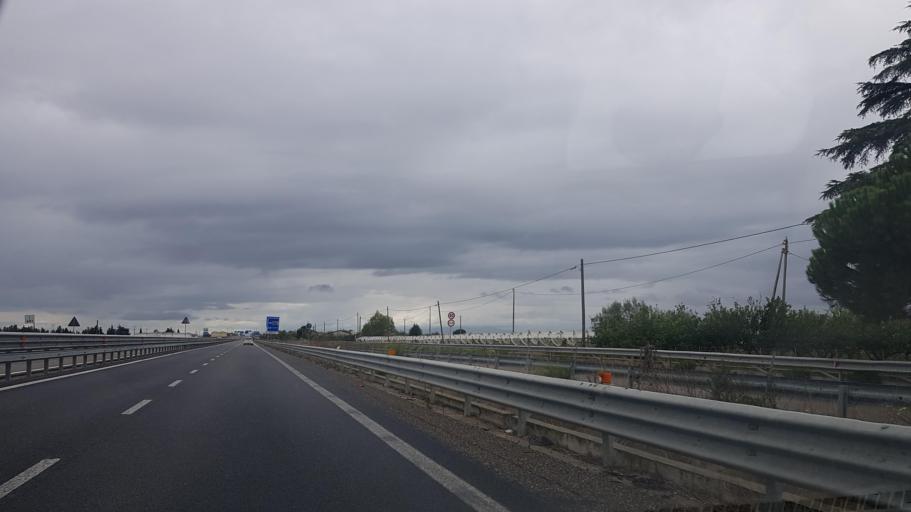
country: IT
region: Apulia
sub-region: Provincia di Taranto
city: Marina di Ginosa
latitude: 40.4108
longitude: 16.8123
